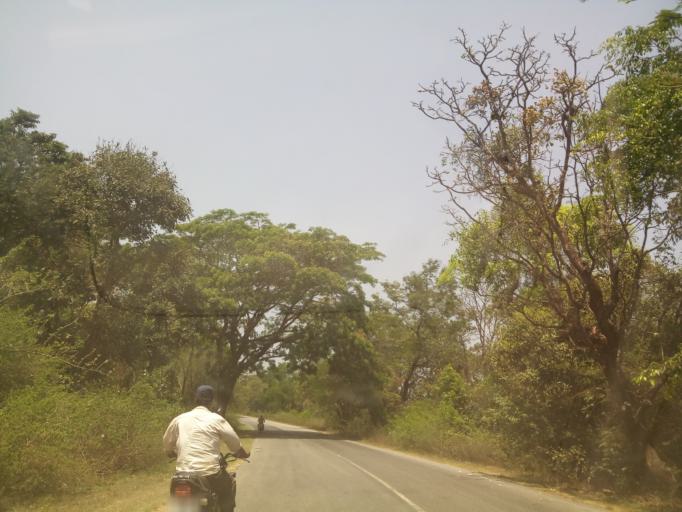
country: IN
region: Karnataka
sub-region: Hassan
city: Sakleshpur
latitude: 12.9537
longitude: 75.8653
